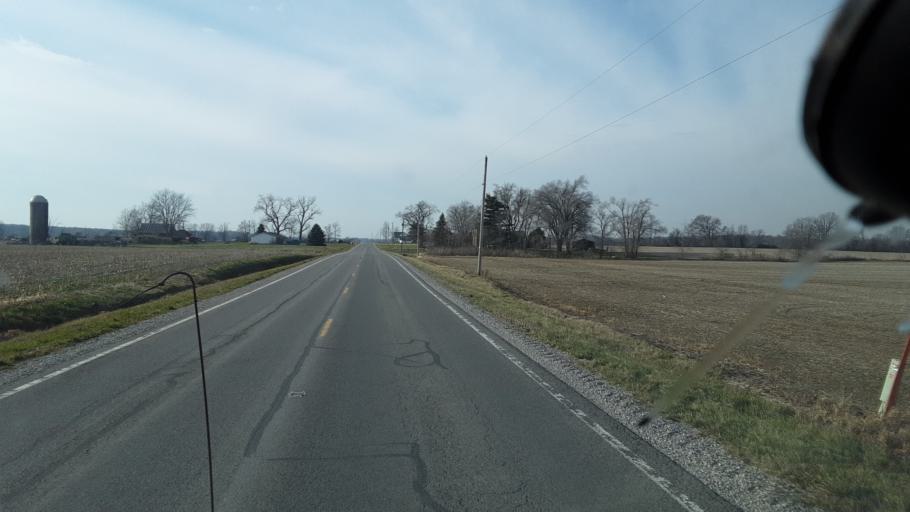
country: US
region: Ohio
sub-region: Williams County
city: Edgerton
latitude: 41.3827
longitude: -84.7535
